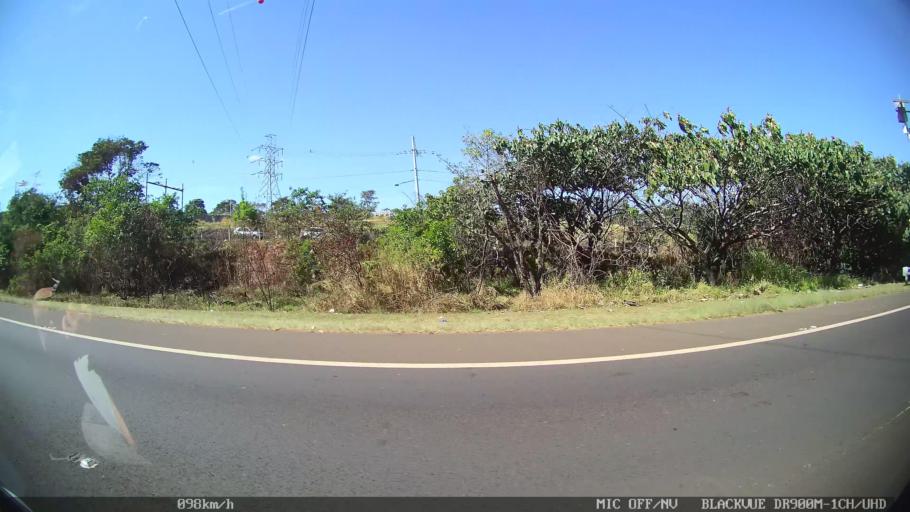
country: BR
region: Sao Paulo
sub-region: Franca
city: Franca
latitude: -20.5202
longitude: -47.4179
